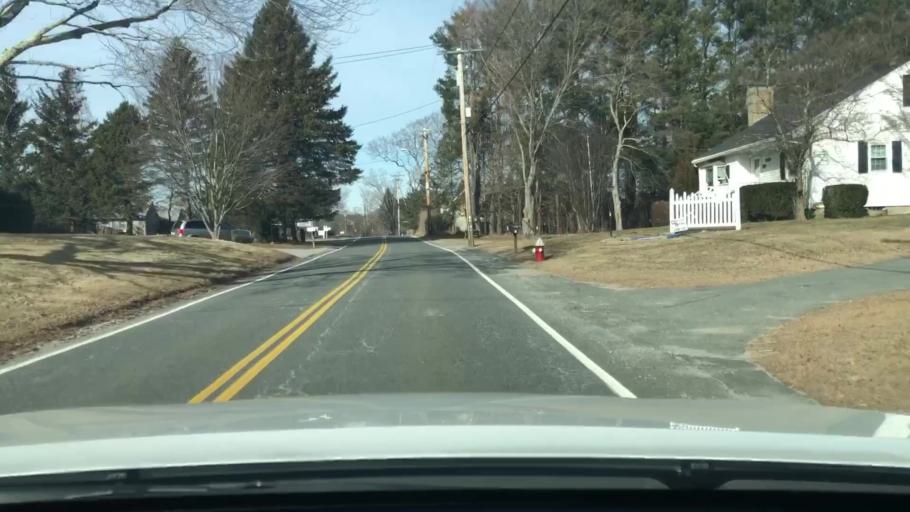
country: US
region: Massachusetts
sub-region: Worcester County
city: Blackstone
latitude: 42.0509
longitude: -71.5208
